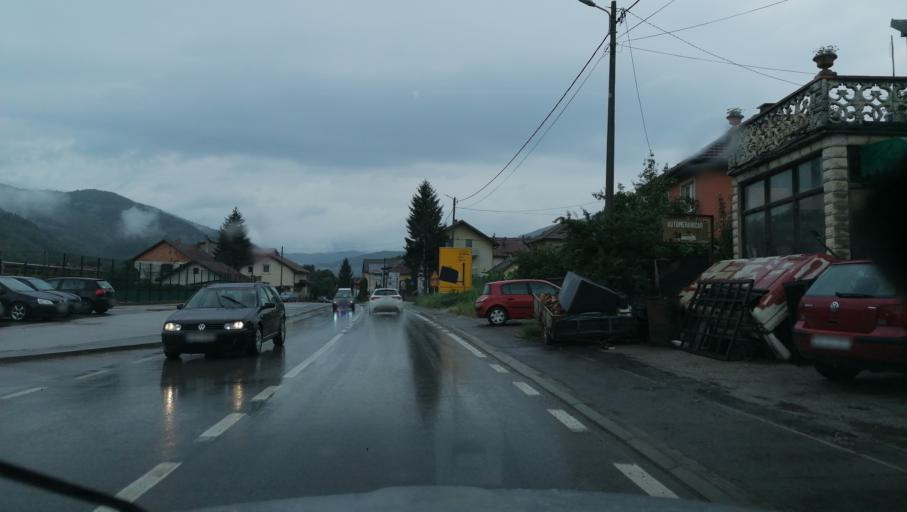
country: BA
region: Federation of Bosnia and Herzegovina
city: Gorazde
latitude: 43.6730
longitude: 18.9826
